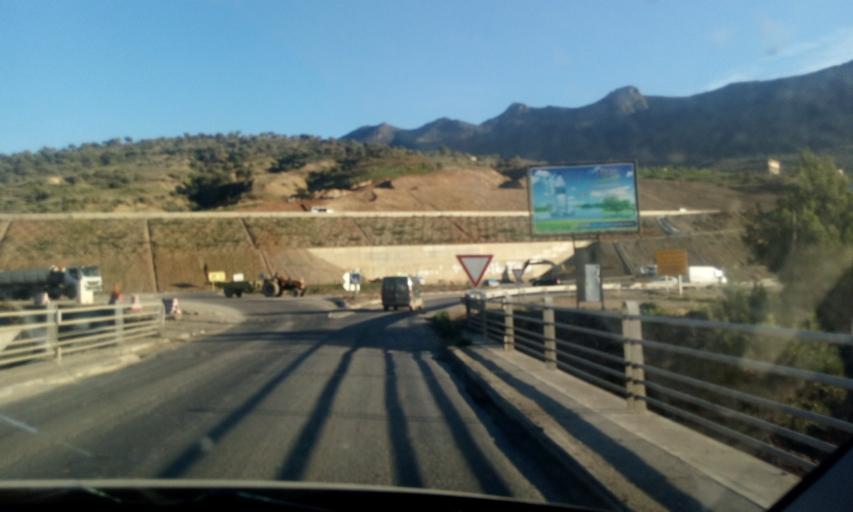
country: DZ
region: Bejaia
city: Akbou
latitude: 36.4803
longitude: 4.5936
